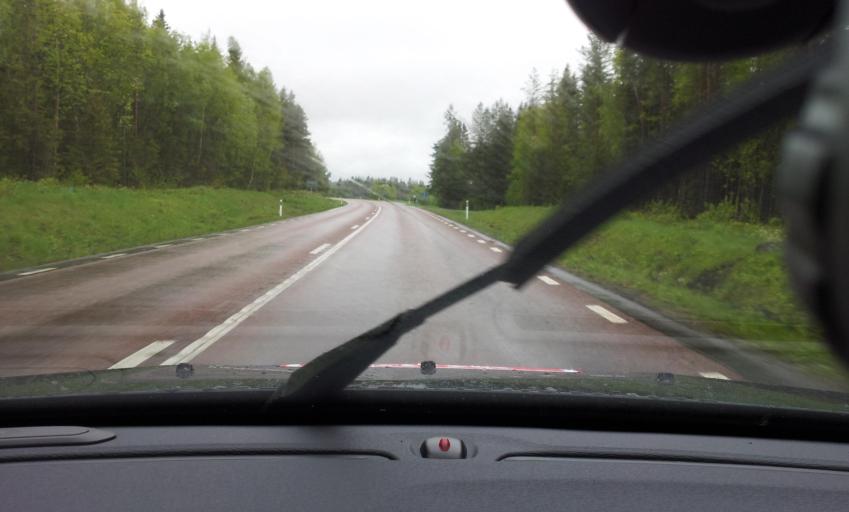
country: SE
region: Jaemtland
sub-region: Bergs Kommun
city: Hoverberg
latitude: 62.9045
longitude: 14.5221
